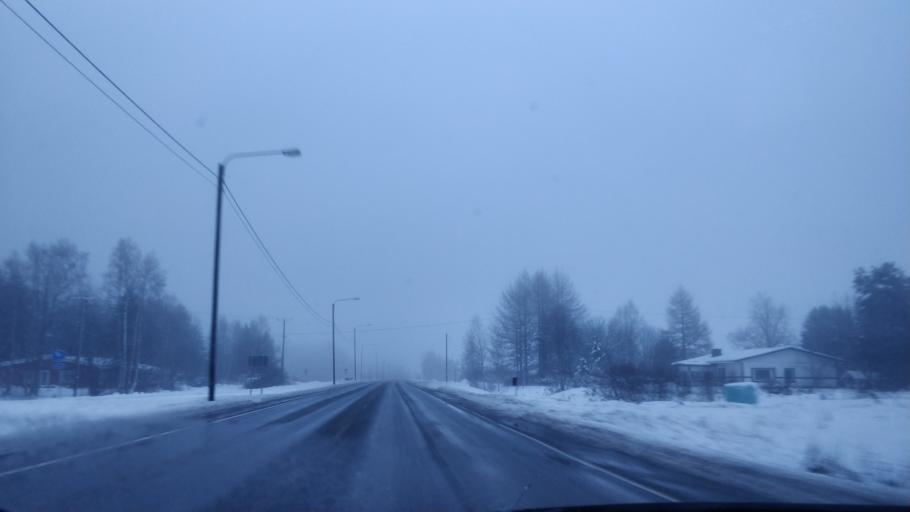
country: FI
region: Lapland
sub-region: Kemi-Tornio
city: Tervola
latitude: 66.1469
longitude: 24.9678
